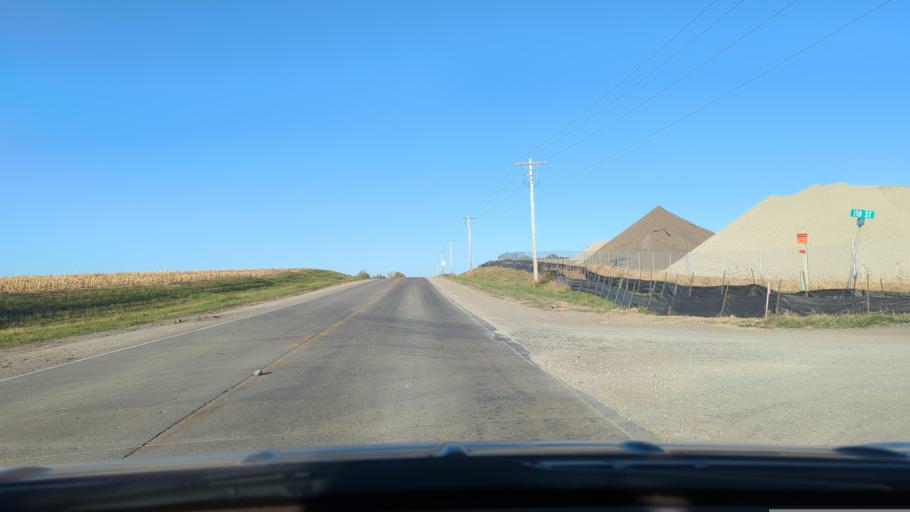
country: US
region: Nebraska
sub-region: Sarpy County
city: Springfield
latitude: 41.1032
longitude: -96.1480
